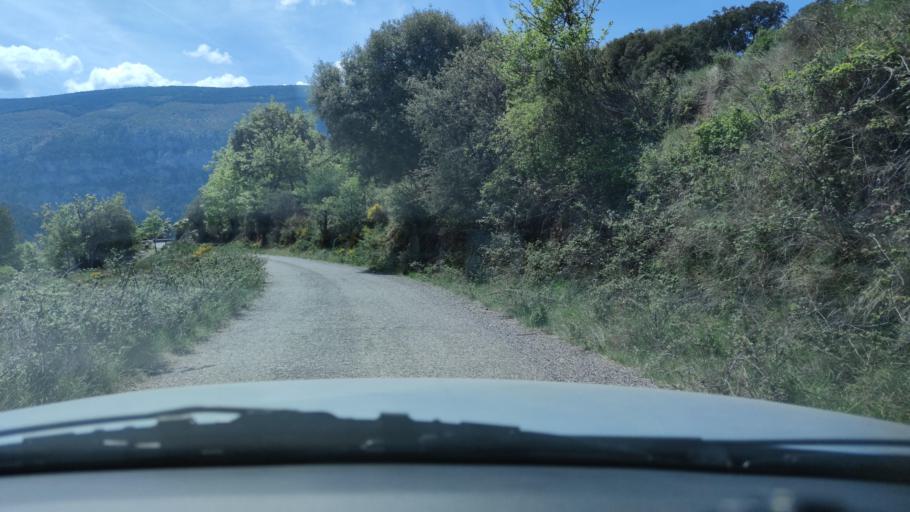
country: ES
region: Catalonia
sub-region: Provincia de Lleida
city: Sort
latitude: 42.3166
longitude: 1.0857
